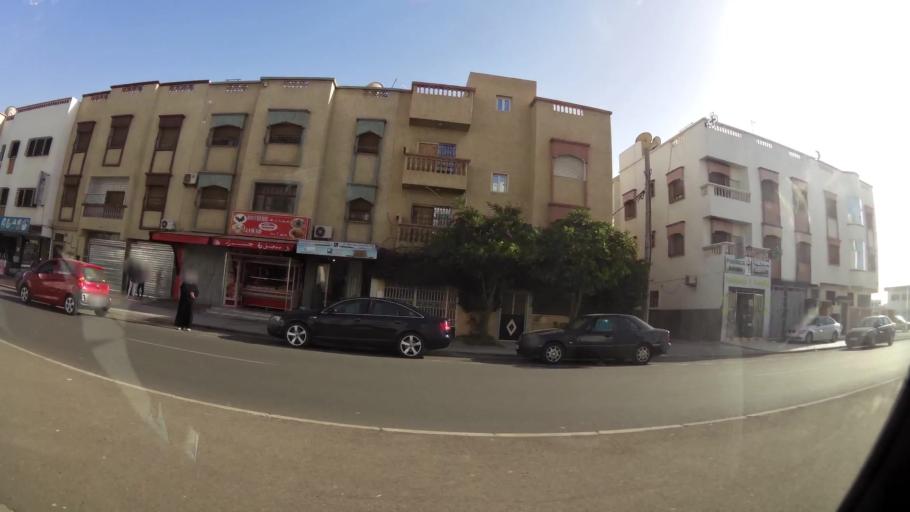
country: MA
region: Oued ed Dahab-Lagouira
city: Dakhla
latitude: 30.3956
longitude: -9.5416
